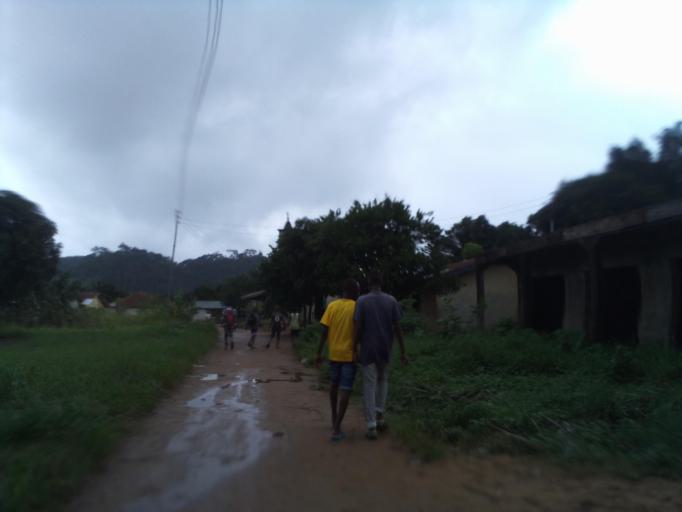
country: SL
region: Eastern Province
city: Kenema
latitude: 7.8517
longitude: -11.2107
